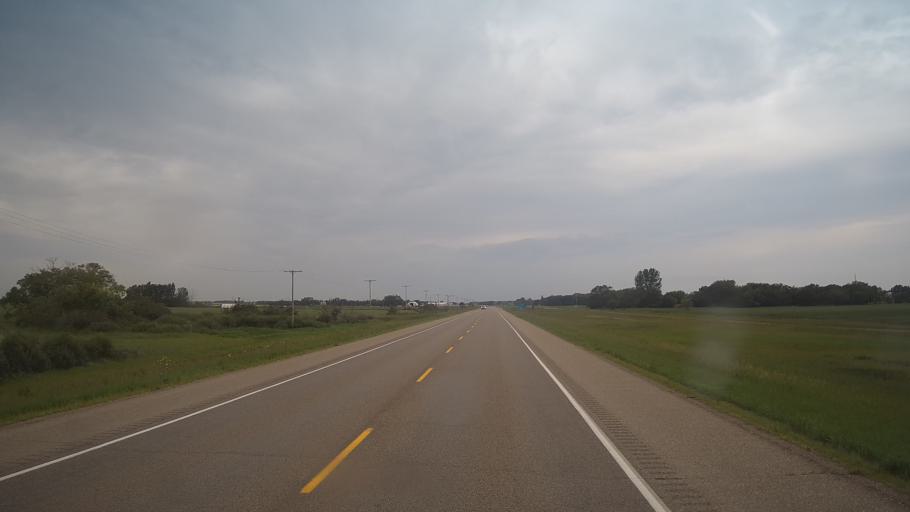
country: CA
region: Saskatchewan
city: Langham
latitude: 52.1290
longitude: -107.2088
